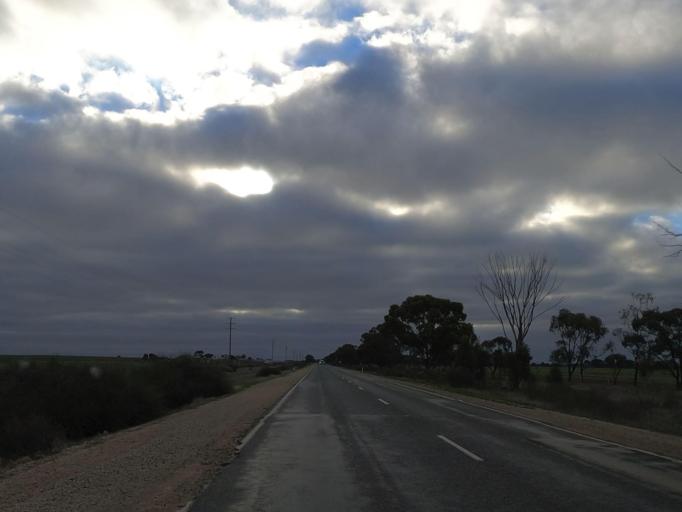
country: AU
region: Victoria
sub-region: Swan Hill
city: Swan Hill
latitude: -35.6463
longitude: 143.8351
